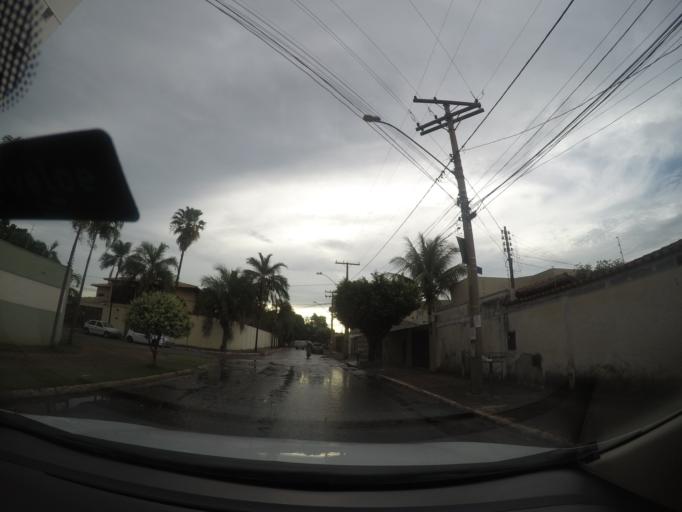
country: BR
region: Goias
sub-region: Goiania
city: Goiania
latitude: -16.6850
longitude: -49.3003
